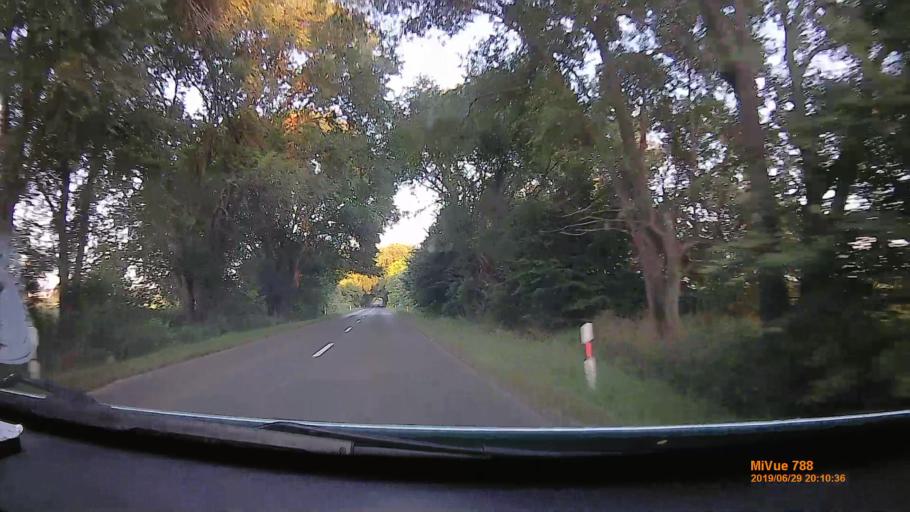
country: HU
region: Pest
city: Telki
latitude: 47.5340
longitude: 18.7783
